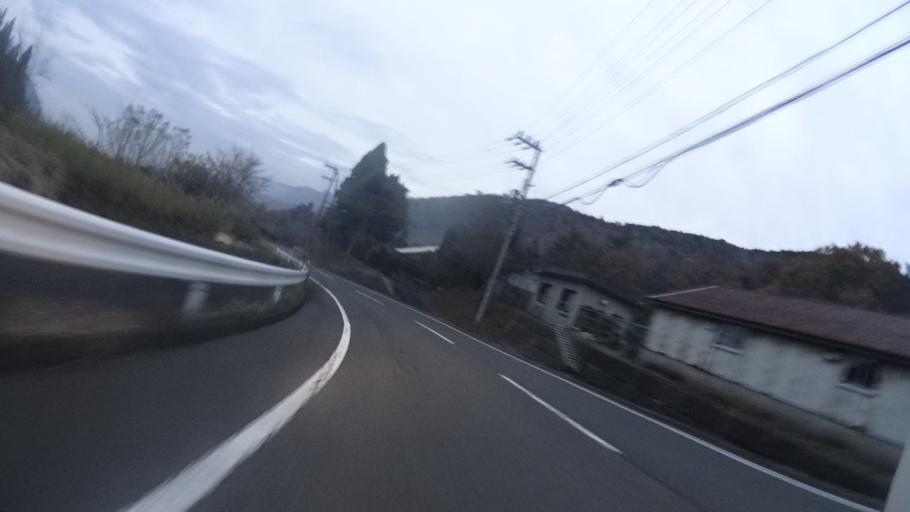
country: JP
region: Kyoto
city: Maizuru
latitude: 35.5347
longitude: 135.3954
